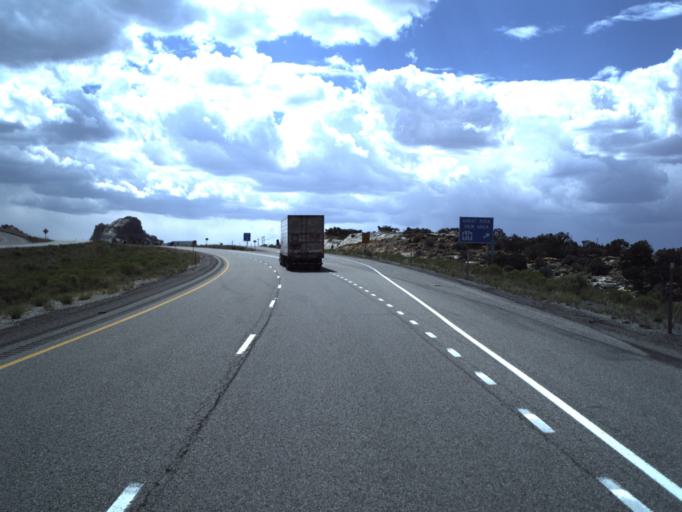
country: US
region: Utah
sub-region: Emery County
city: Ferron
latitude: 38.8660
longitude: -110.8086
